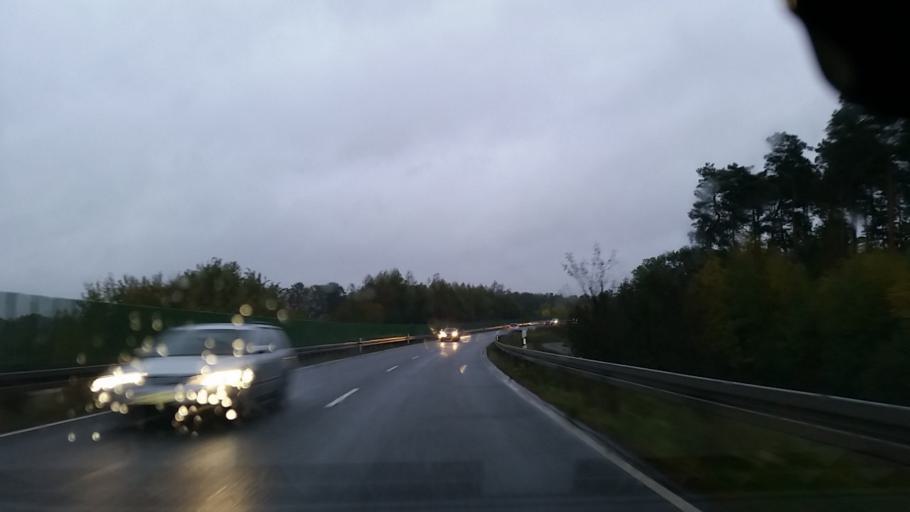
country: DE
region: Lower Saxony
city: Osloss
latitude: 52.4232
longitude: 10.6755
